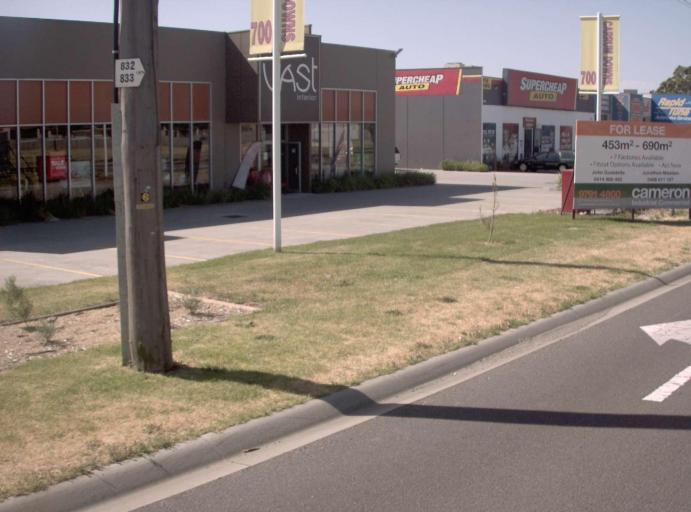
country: AU
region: Victoria
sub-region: Frankston
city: Carrum Downs
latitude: -38.0873
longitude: 145.1820
